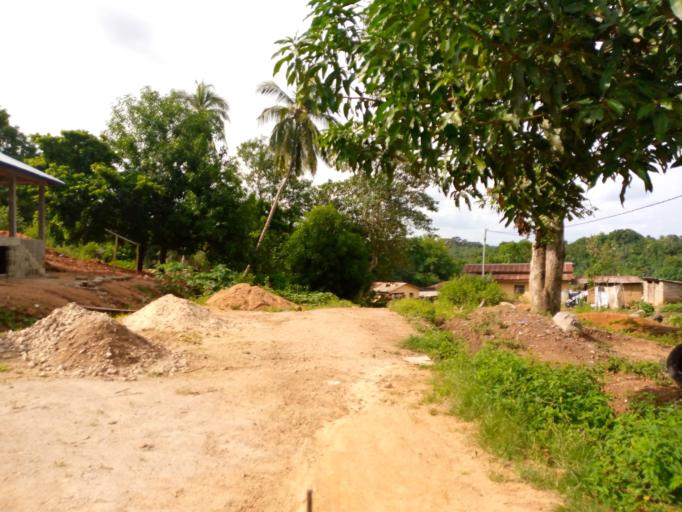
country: SL
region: Northern Province
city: Magburaka
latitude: 8.7229
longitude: -11.9555
